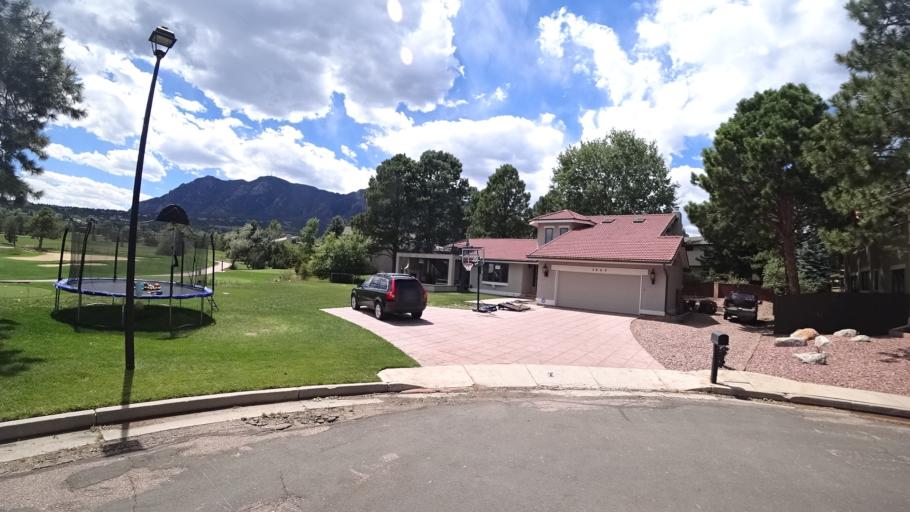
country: US
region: Colorado
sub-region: El Paso County
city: Stratmoor
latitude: 38.7822
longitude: -104.8278
